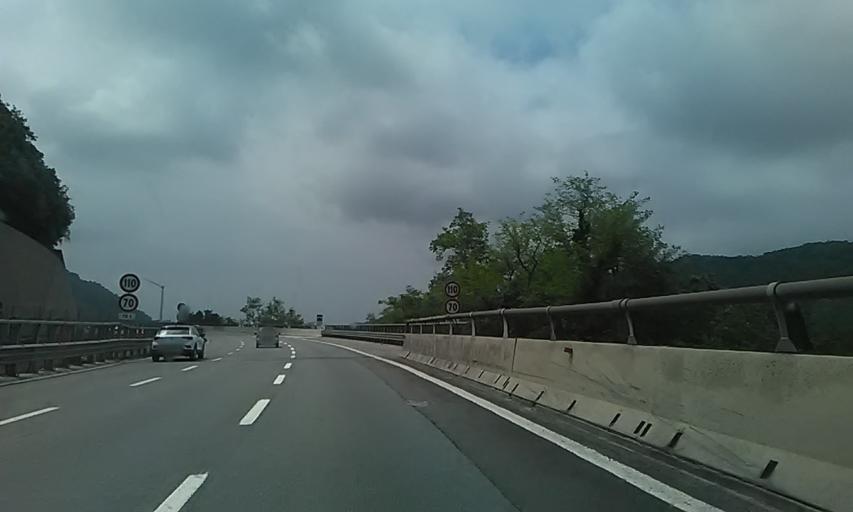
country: IT
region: Liguria
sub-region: Provincia di Genova
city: Masone
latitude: 44.4756
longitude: 8.7351
